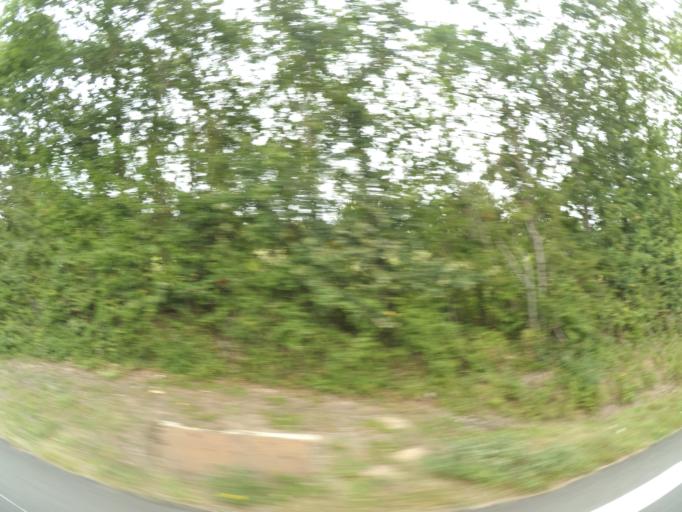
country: FR
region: Pays de la Loire
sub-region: Departement de la Vendee
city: Froidfond
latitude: 46.8630
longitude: -1.7895
